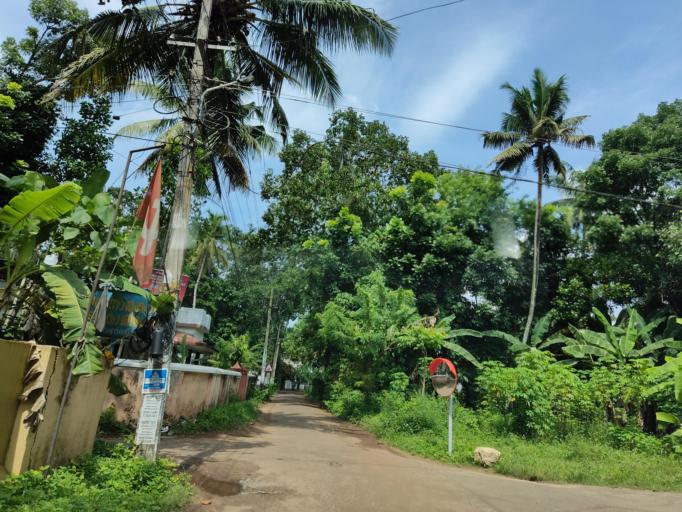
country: IN
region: Kerala
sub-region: Alappuzha
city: Mavelikara
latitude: 9.2601
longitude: 76.5631
